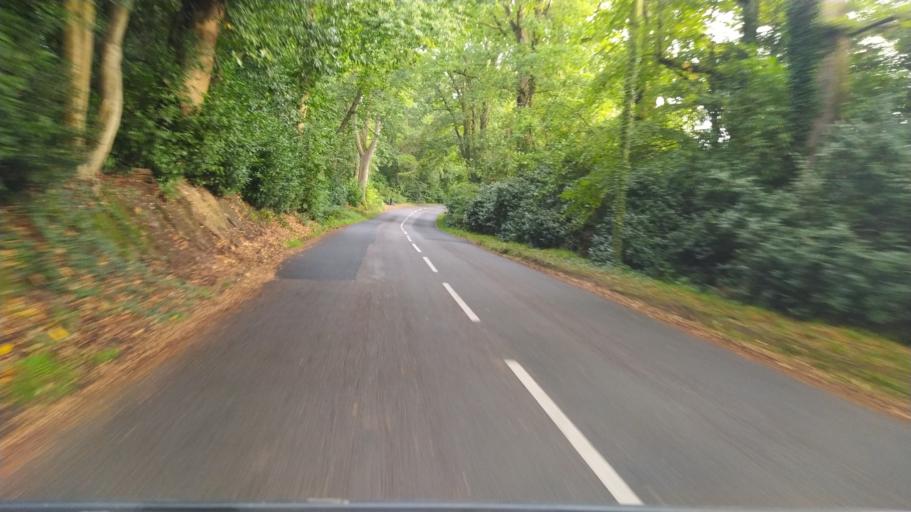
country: GB
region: England
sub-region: Hampshire
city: West Wellow
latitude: 51.0056
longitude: -1.5480
